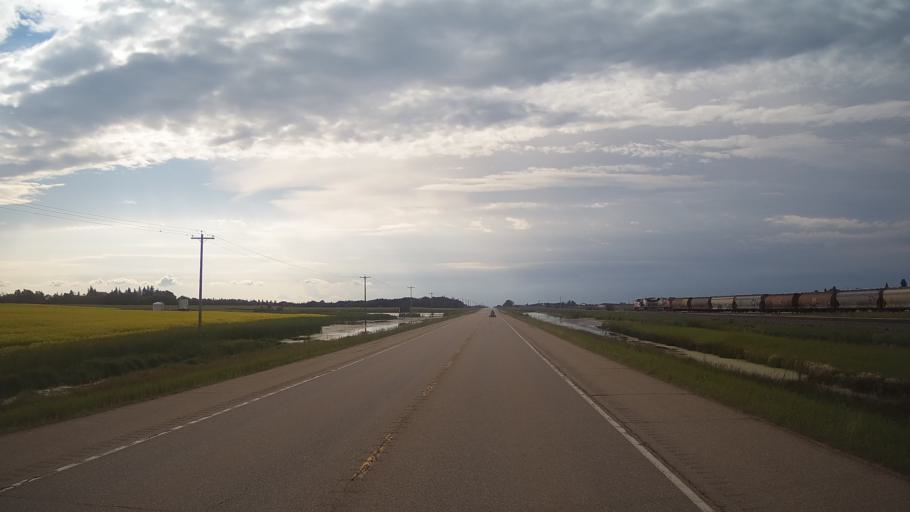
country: CA
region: Alberta
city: Viking
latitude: 53.0997
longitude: -111.8026
